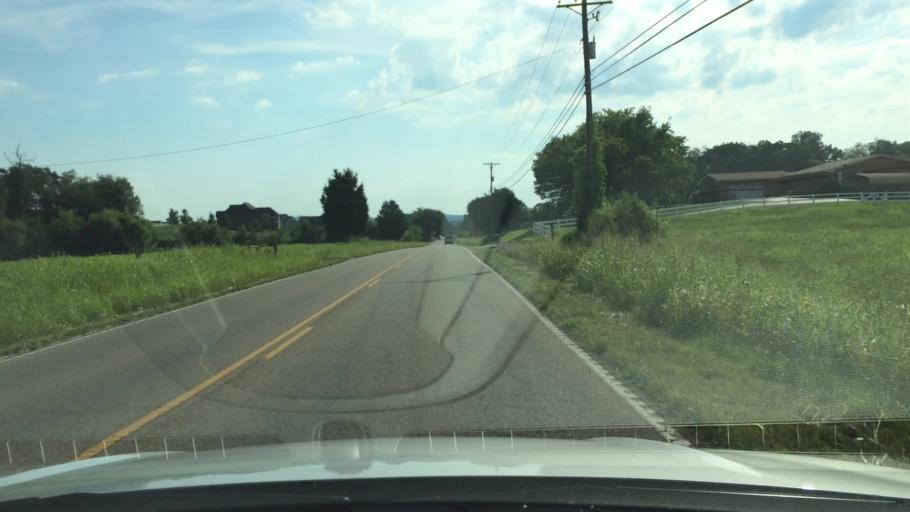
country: US
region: Tennessee
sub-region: Sevier County
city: Seymour
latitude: 35.9080
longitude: -83.6897
